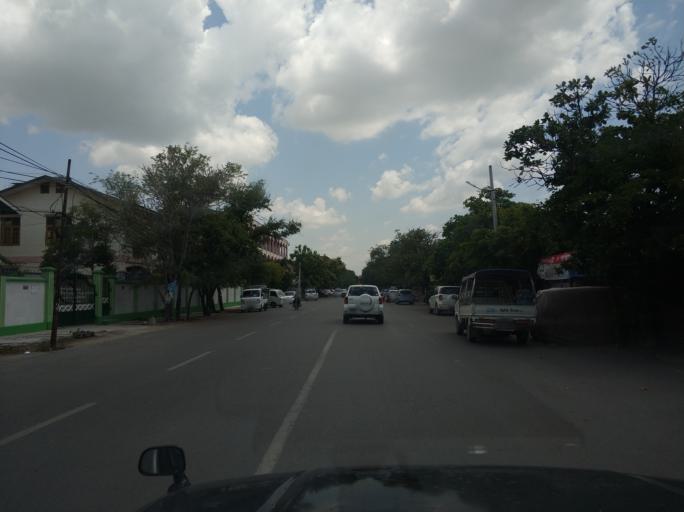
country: MM
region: Mandalay
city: Mandalay
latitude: 21.9776
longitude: 96.1035
